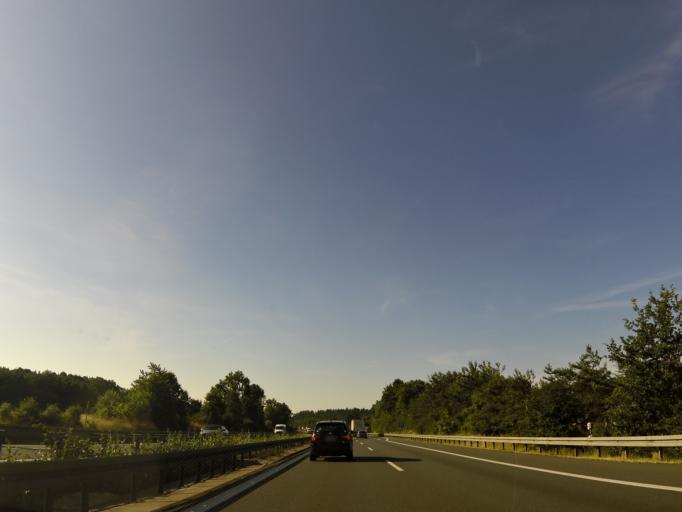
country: DE
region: Bavaria
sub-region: Regierungsbezirk Mittelfranken
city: Hessdorf
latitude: 49.6239
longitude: 10.9196
